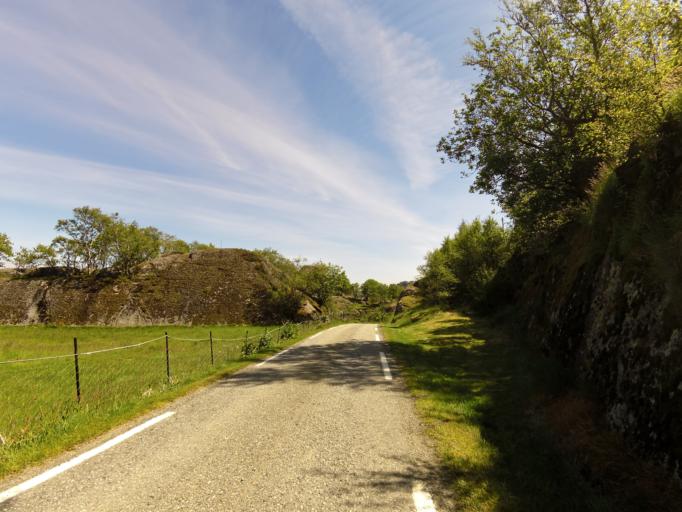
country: NO
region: Rogaland
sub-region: Sokndal
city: Hauge i Dalane
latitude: 58.3563
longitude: 6.1559
